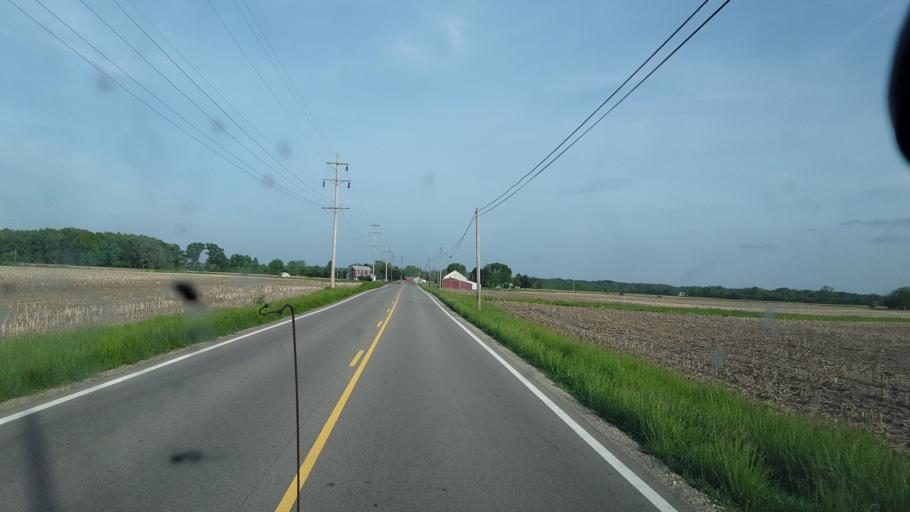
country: US
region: Ohio
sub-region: Pickaway County
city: Logan Elm Village
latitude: 39.5520
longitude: -82.8622
